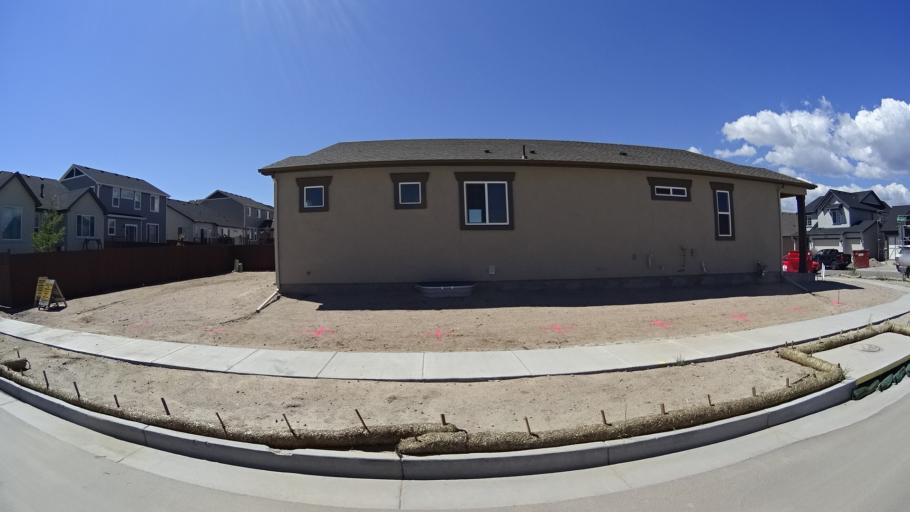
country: US
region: Colorado
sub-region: El Paso County
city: Gleneagle
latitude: 38.9946
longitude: -104.7720
